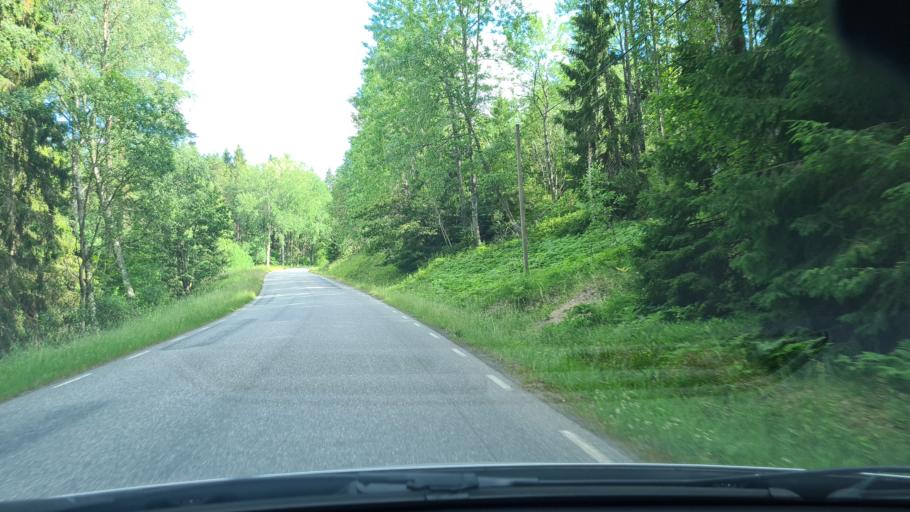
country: SE
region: Stockholm
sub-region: Varmdo Kommun
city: Mortnas
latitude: 59.3999
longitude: 18.4633
